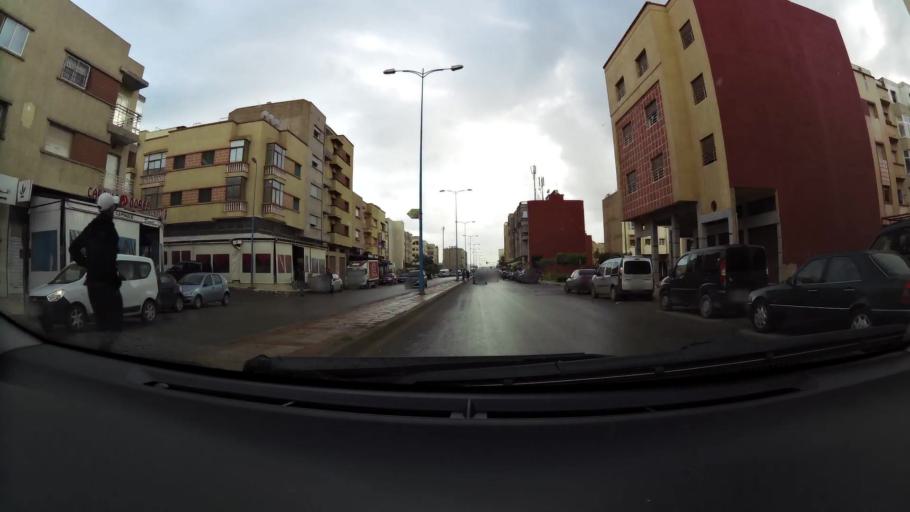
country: MA
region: Grand Casablanca
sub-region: Mohammedia
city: Mohammedia
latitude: 33.6801
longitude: -7.3849
